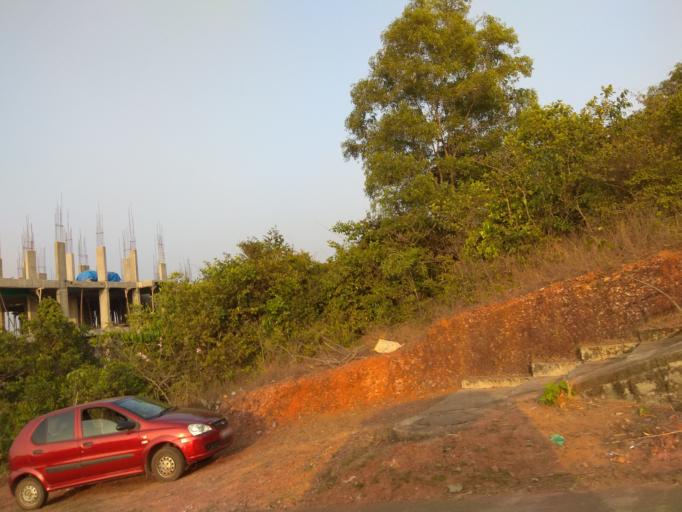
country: IN
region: Karnataka
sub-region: Dakshina Kannada
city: Mangalore
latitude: 12.9161
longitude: 74.8593
